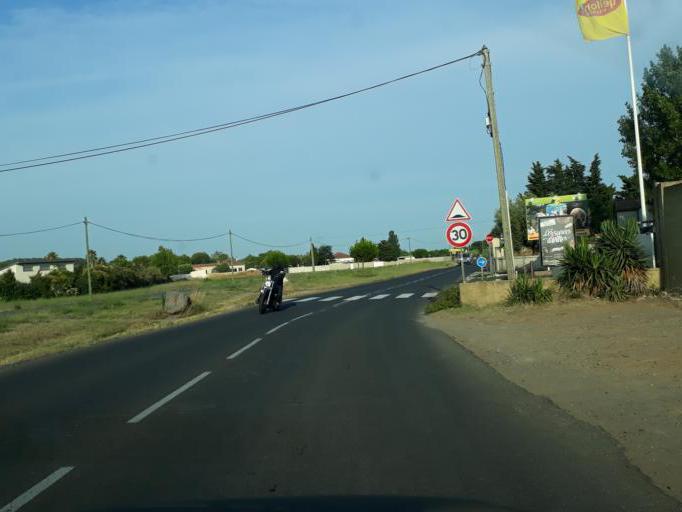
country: FR
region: Languedoc-Roussillon
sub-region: Departement de l'Herault
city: Agde
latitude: 43.2870
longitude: 3.4781
